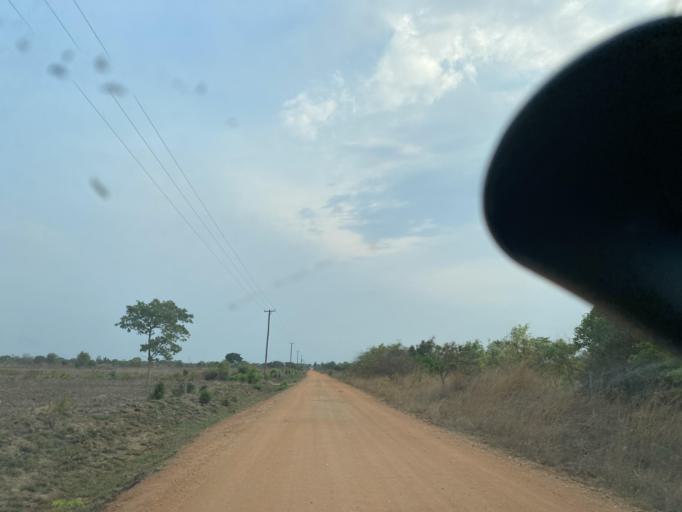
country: ZM
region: Lusaka
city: Chongwe
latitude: -15.2060
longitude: 28.5807
